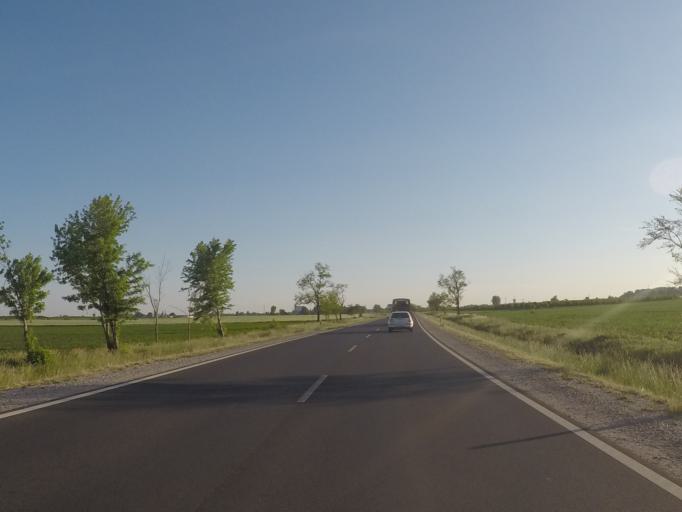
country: HU
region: Heves
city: Heves
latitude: 47.6231
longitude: 20.3186
